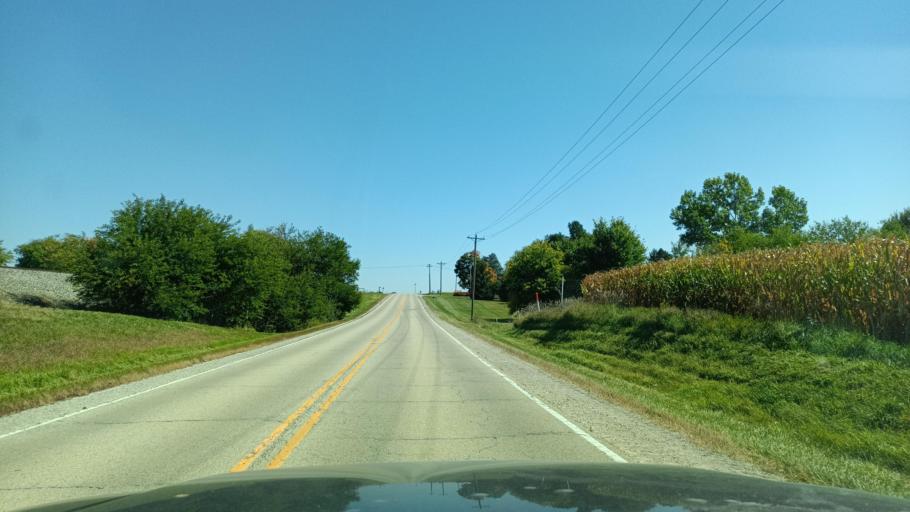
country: US
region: Illinois
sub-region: Woodford County
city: Eureka
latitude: 40.6269
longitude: -89.3022
